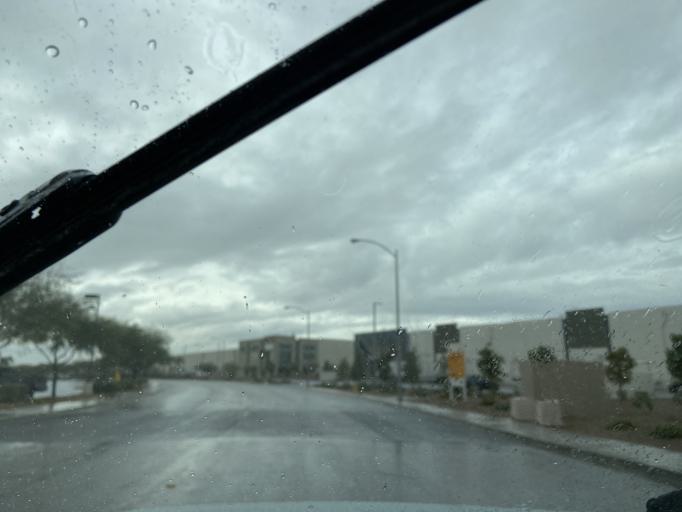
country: US
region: Nevada
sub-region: Clark County
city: Sunrise Manor
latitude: 36.2379
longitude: -115.1003
